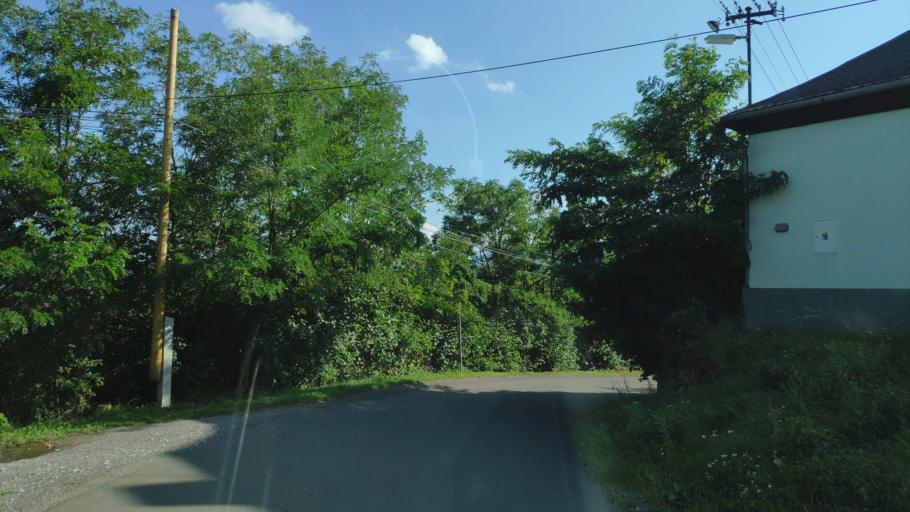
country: SK
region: Kosicky
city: Secovce
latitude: 48.6350
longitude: 21.4765
